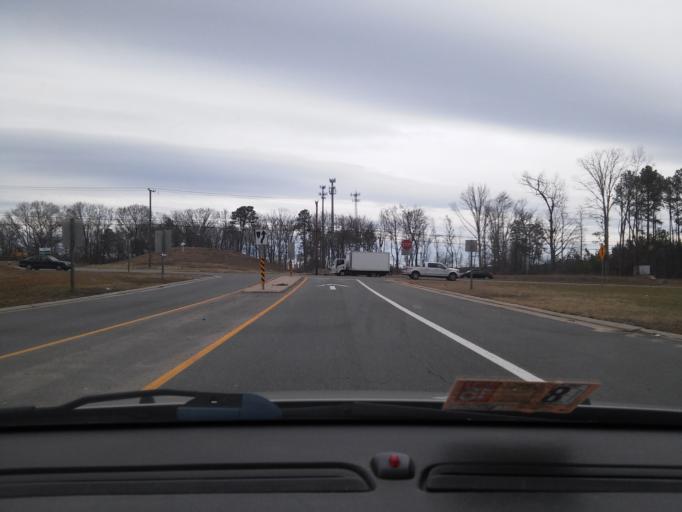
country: US
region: Virginia
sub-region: Henrico County
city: Short Pump
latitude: 37.6629
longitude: -77.6534
